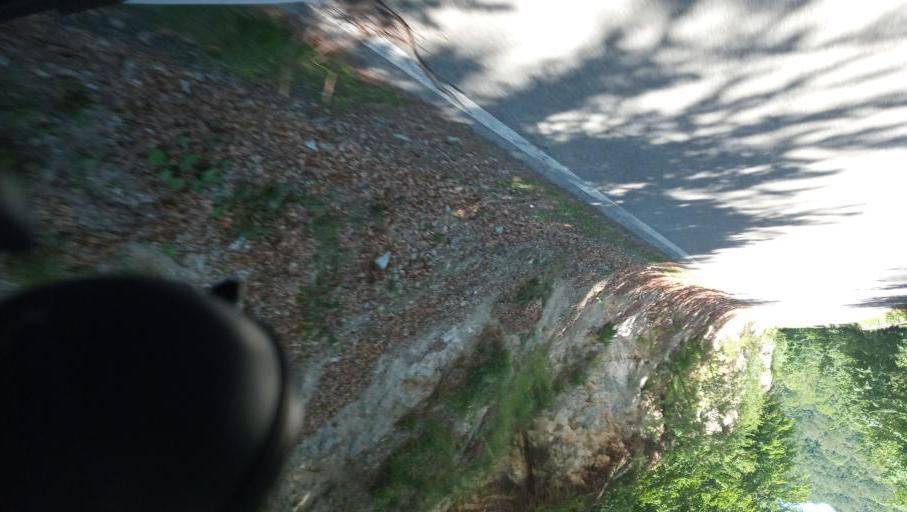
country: RO
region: Mehedinti
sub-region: Comuna Isverna
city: Isverna
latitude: 45.0409
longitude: 22.6204
